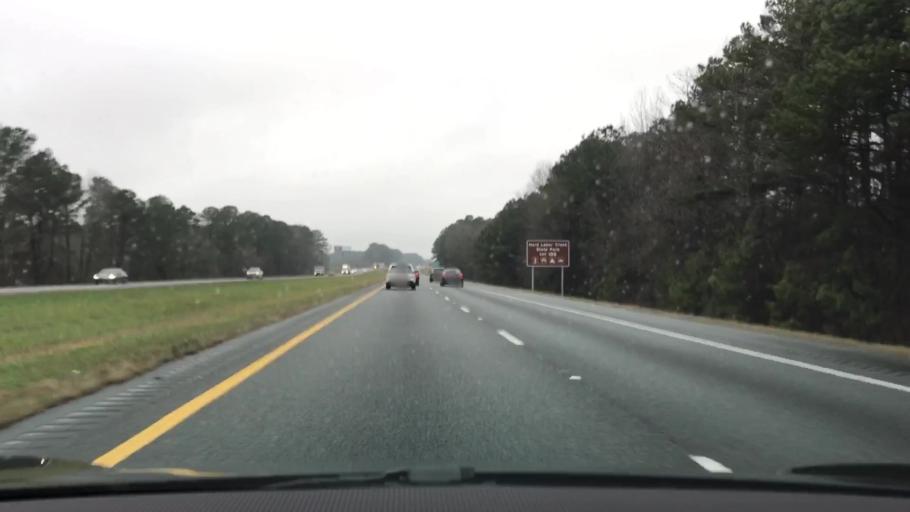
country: US
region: Georgia
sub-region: Walton County
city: Social Circle
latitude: 33.5878
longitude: -83.6133
